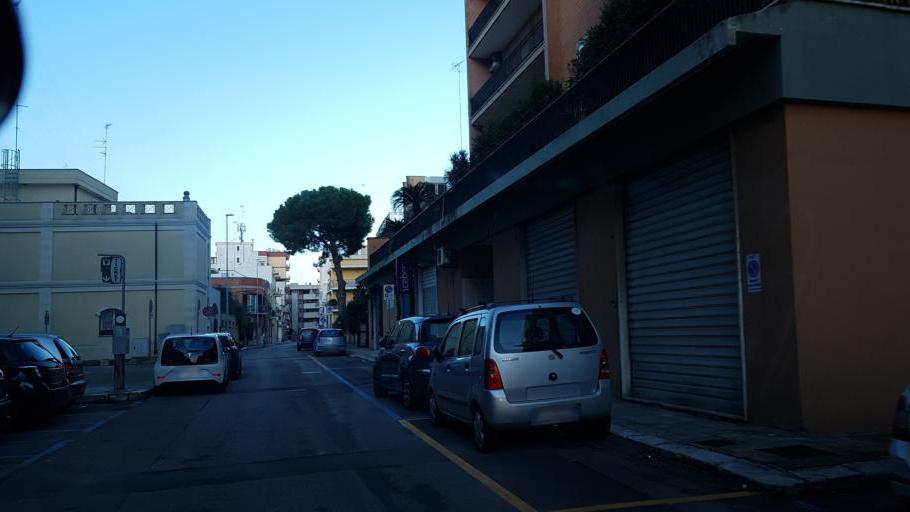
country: IT
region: Apulia
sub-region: Provincia di Lecce
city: Lecce
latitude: 40.3602
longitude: 18.1768
